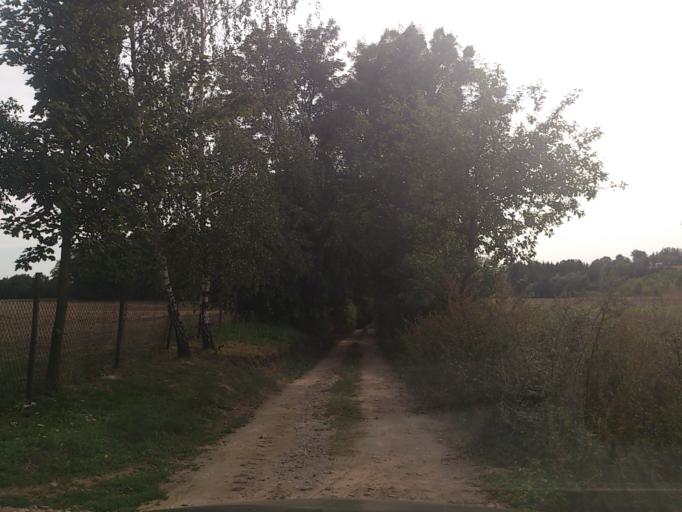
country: PL
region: Kujawsko-Pomorskie
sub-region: Powiat golubsko-dobrzynski
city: Golub-Dobrzyn
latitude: 53.1266
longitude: 19.0644
